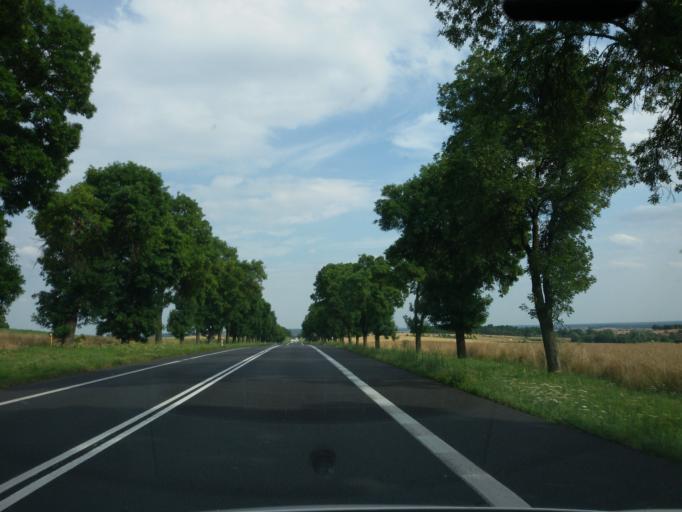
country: PL
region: Lower Silesian Voivodeship
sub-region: Powiat polkowicki
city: Gaworzyce
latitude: 51.6411
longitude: 15.8803
